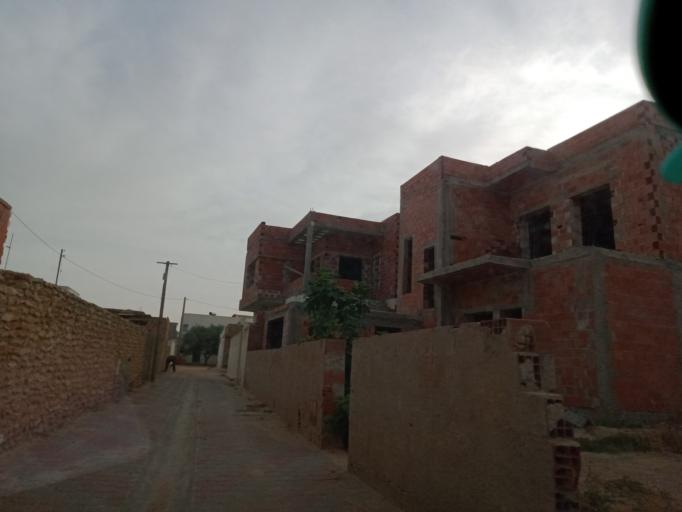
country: TN
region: Safaqis
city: Al Qarmadah
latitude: 34.8063
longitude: 10.7529
